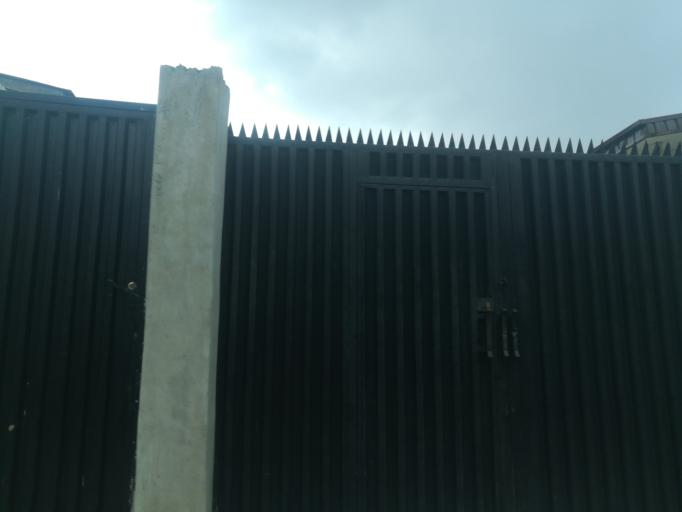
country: NG
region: Oyo
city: Ibadan
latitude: 7.3516
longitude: 3.8737
